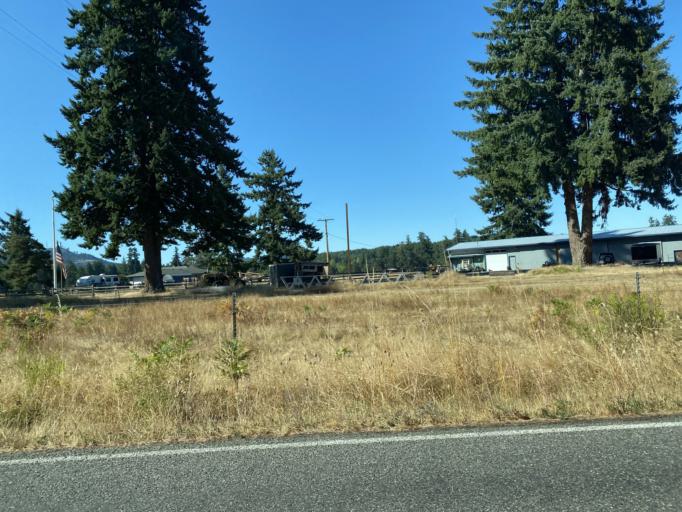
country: US
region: Washington
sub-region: Thurston County
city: Rainier
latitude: 46.8872
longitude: -122.7464
